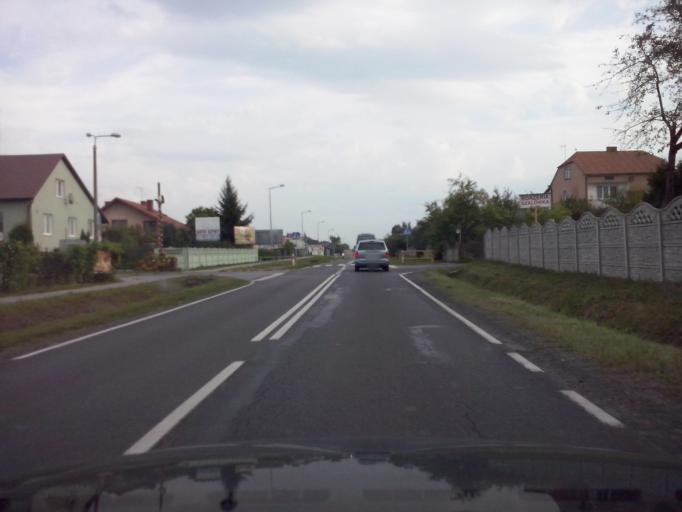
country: PL
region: Lublin Voivodeship
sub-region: Powiat bilgorajski
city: Bilgoraj
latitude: 50.5096
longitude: 22.7188
